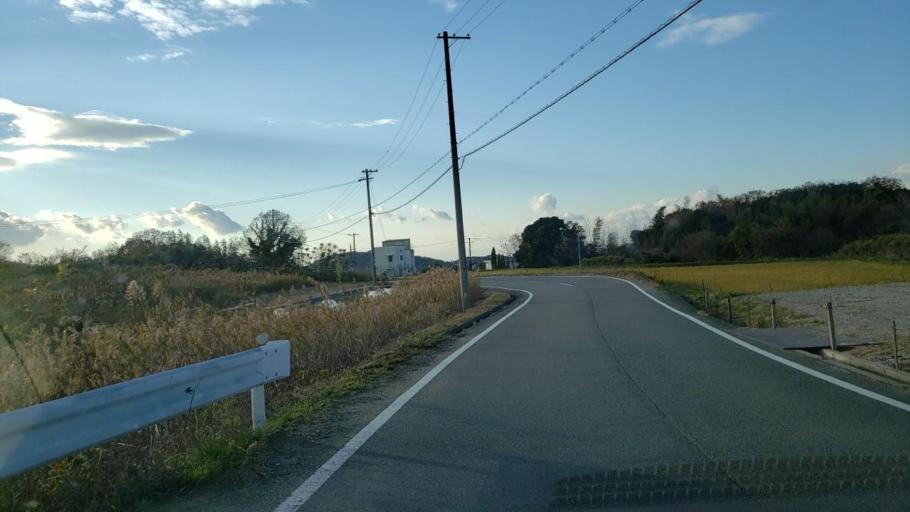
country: JP
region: Hyogo
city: Akashi
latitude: 34.5448
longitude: 134.9707
